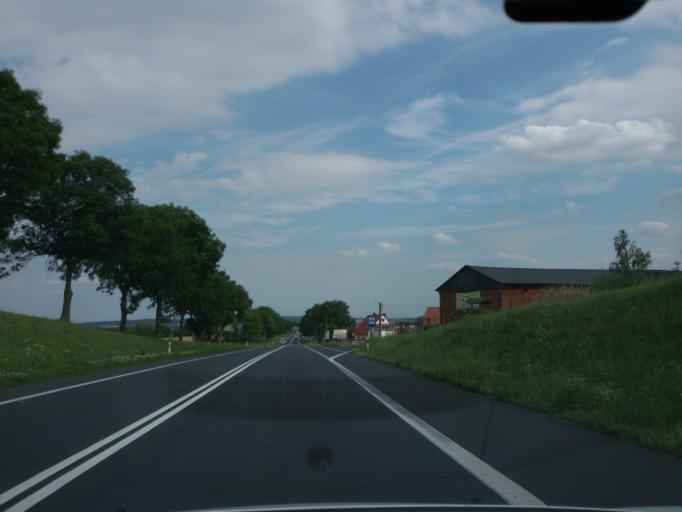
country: PL
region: Lower Silesian Voivodeship
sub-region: Powiat polkowicki
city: Gaworzyce
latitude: 51.6353
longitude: 15.8938
